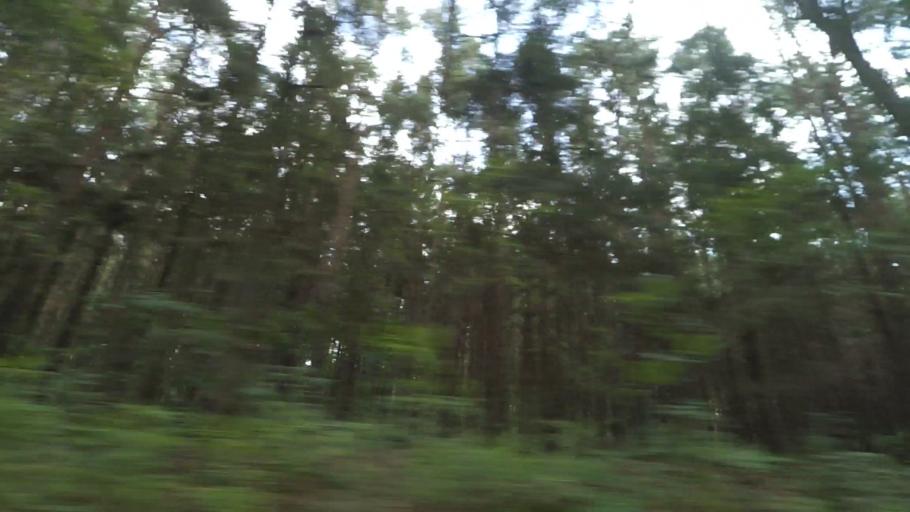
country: DK
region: Central Jutland
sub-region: Syddjurs Kommune
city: Ryomgard
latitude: 56.4790
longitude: 10.4877
